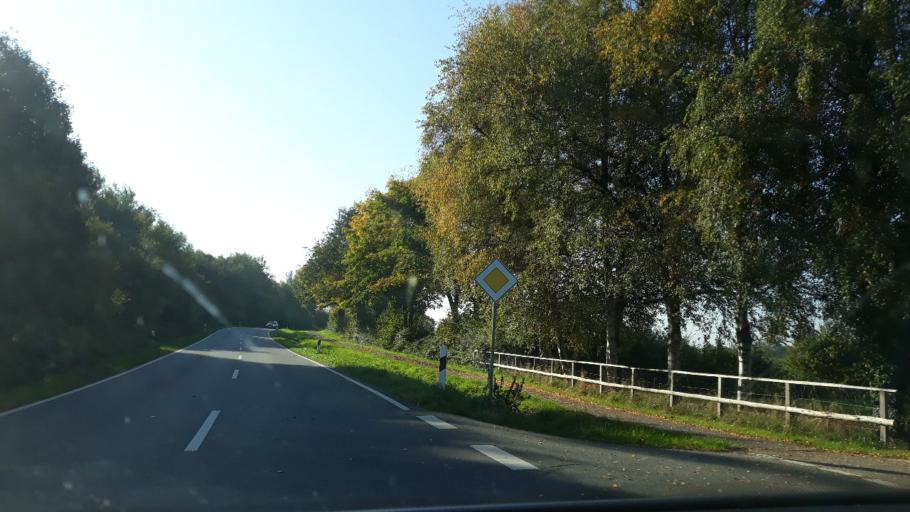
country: DE
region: Schleswig-Holstein
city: Boklund
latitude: 54.6126
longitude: 9.5873
